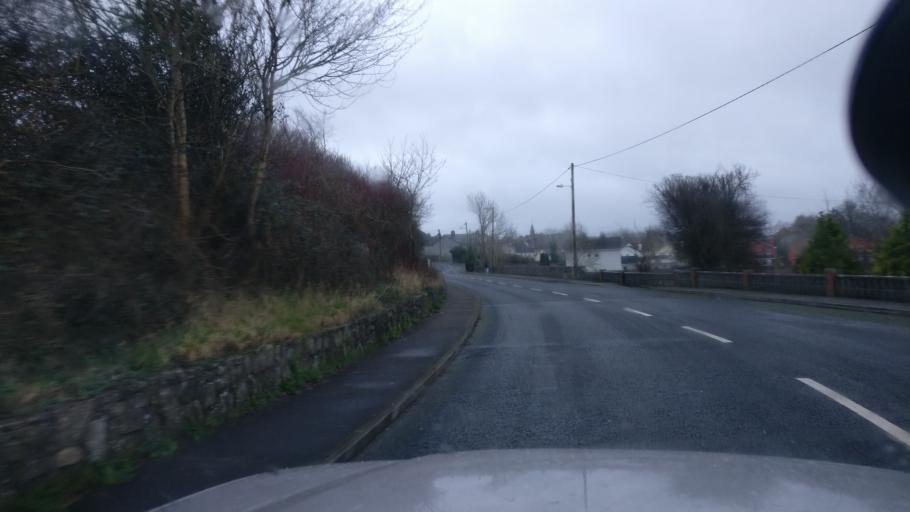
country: IE
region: Connaught
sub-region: County Galway
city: Loughrea
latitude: 53.2023
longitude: -8.5612
